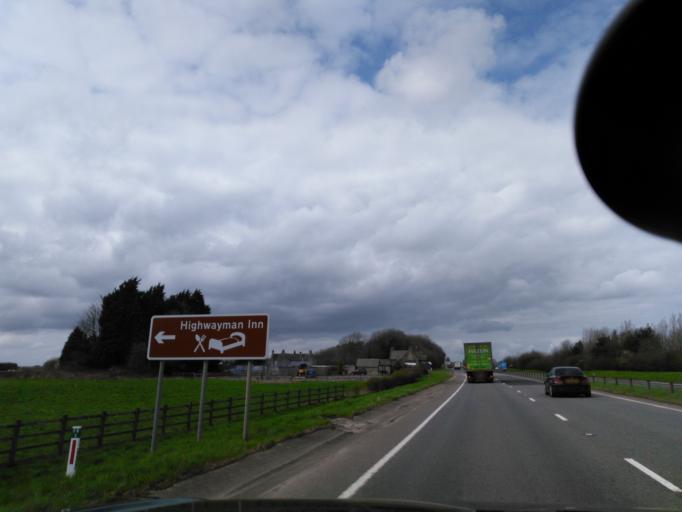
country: GB
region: England
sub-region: Gloucestershire
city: Coates
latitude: 51.7944
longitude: -2.0487
